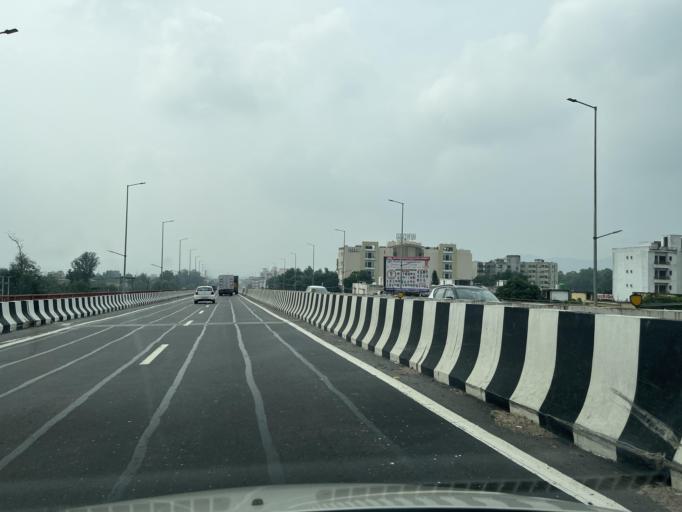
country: IN
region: Uttarakhand
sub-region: Dehradun
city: Raiwala
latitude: 30.0041
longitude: 78.1902
